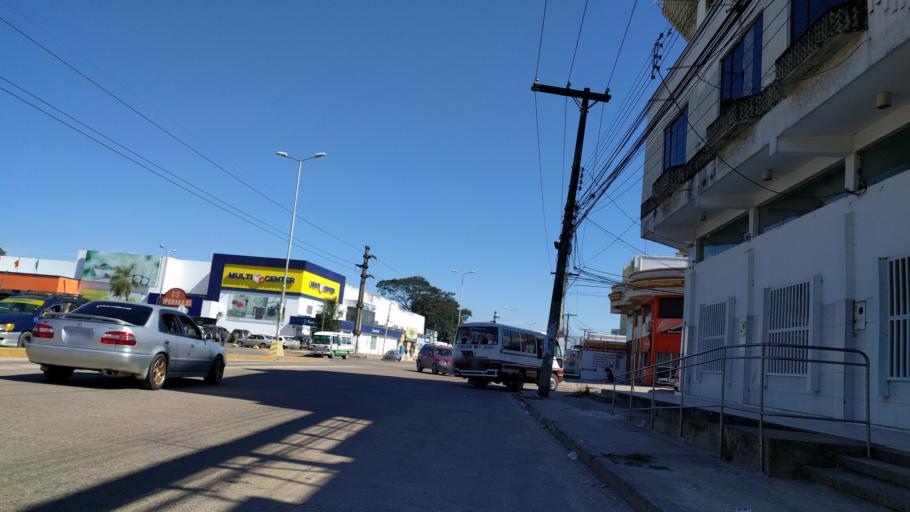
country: BO
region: Santa Cruz
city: Santa Cruz de la Sierra
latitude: -17.8127
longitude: -63.1835
